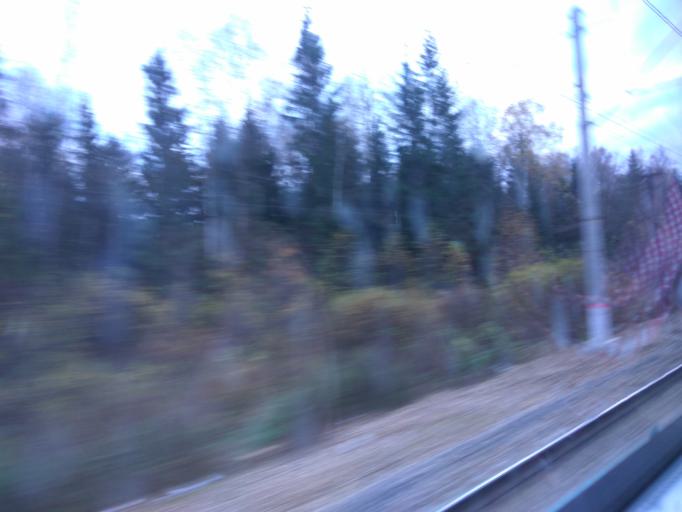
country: RU
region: Moskovskaya
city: Selyatino
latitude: 55.5020
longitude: 36.9420
